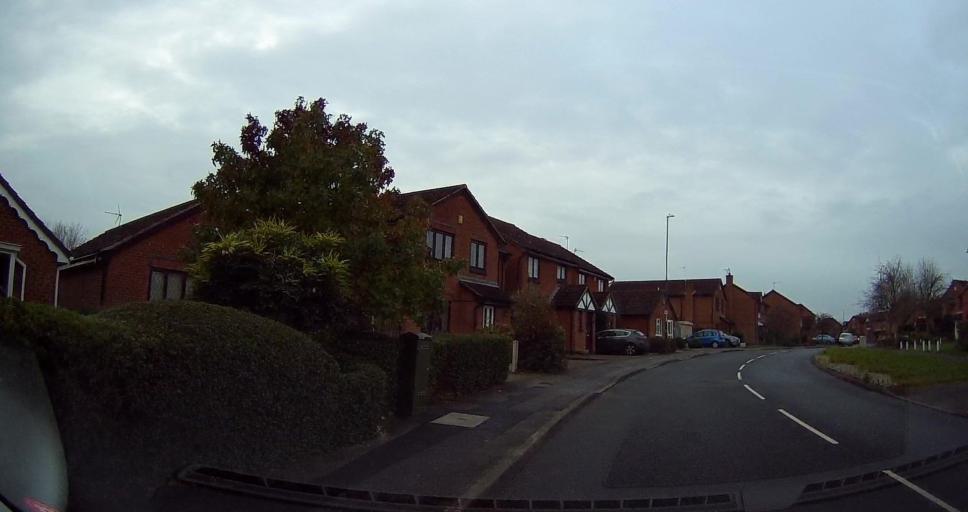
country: GB
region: England
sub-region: Nottinghamshire
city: Kimberley
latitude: 52.9579
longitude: -1.2231
